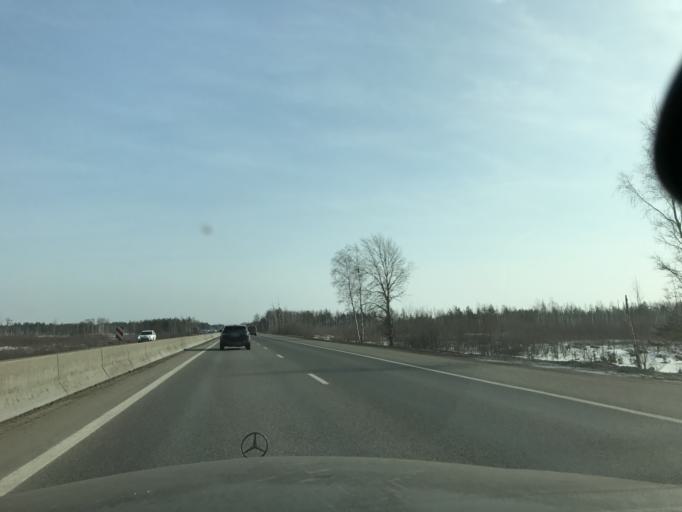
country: RU
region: Nizjnij Novgorod
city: Dzerzhinsk
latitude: 56.3003
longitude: 43.5269
